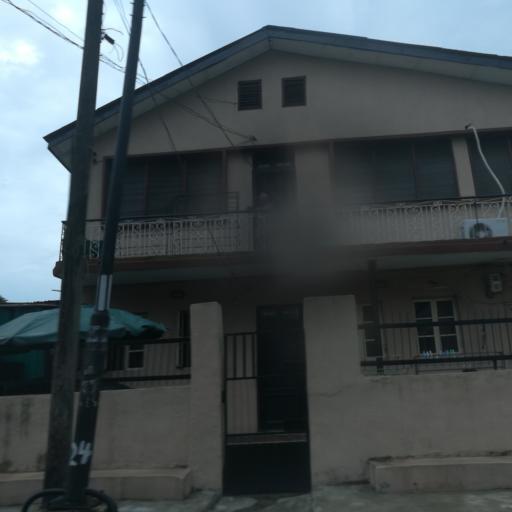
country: NG
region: Lagos
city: Makoko
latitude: 6.4964
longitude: 3.3780
